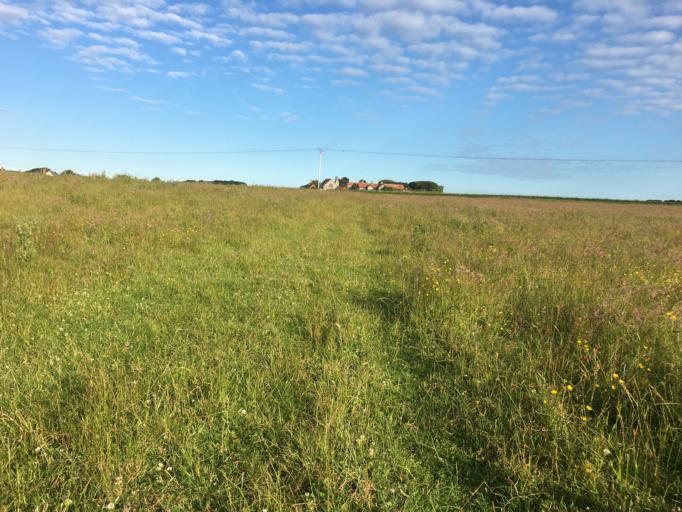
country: GB
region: England
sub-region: Northumberland
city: Bamburgh
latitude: 55.6049
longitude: -1.7046
